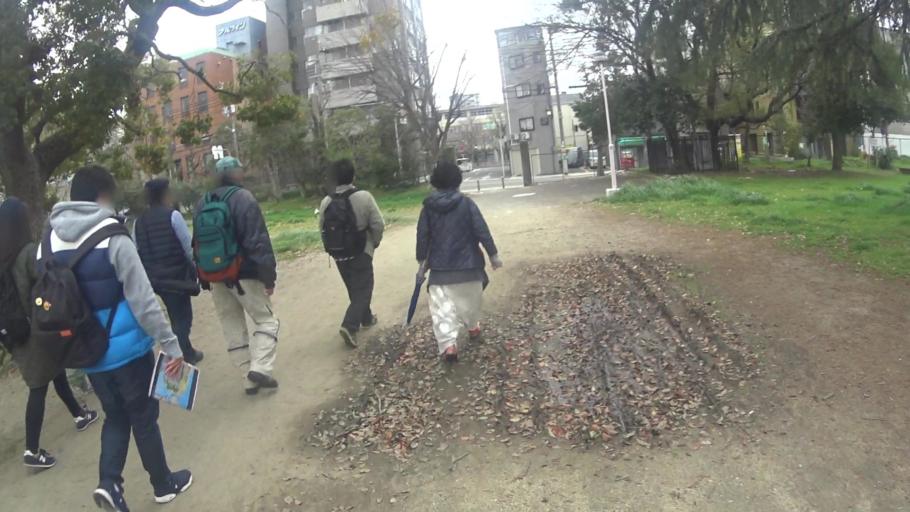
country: JP
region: Osaka
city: Osaka-shi
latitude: 34.6788
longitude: 135.5228
